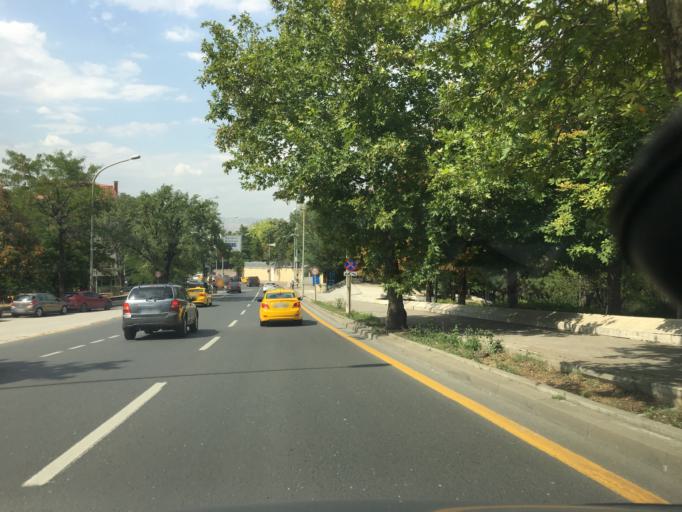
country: TR
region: Ankara
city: Cankaya
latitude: 39.8958
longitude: 32.8619
